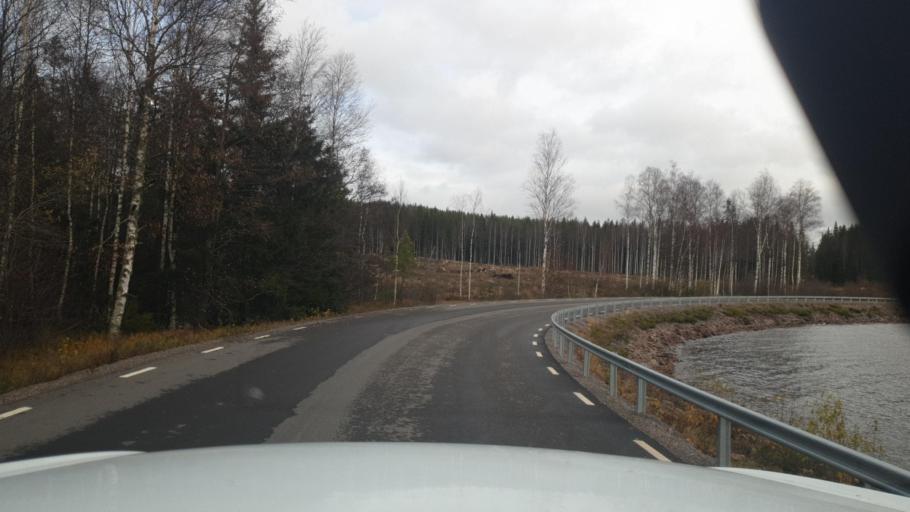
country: SE
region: Vaermland
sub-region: Torsby Kommun
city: Torsby
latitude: 59.9804
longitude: 12.7995
